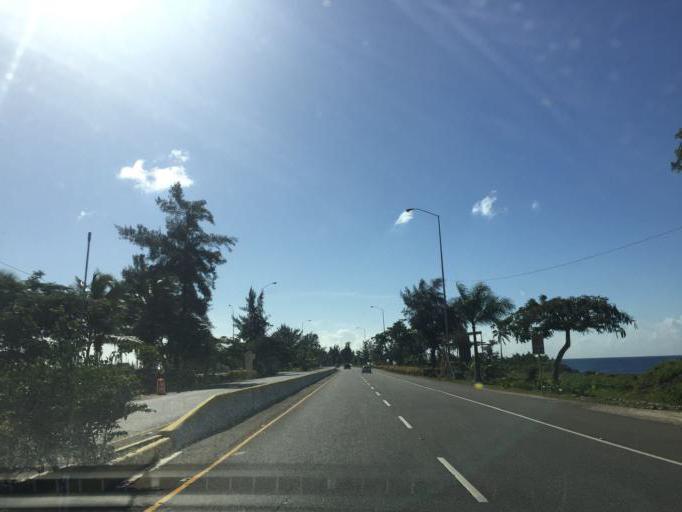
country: DO
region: Santo Domingo
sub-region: Santo Domingo
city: Boca Chica
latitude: 18.4331
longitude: -69.6806
